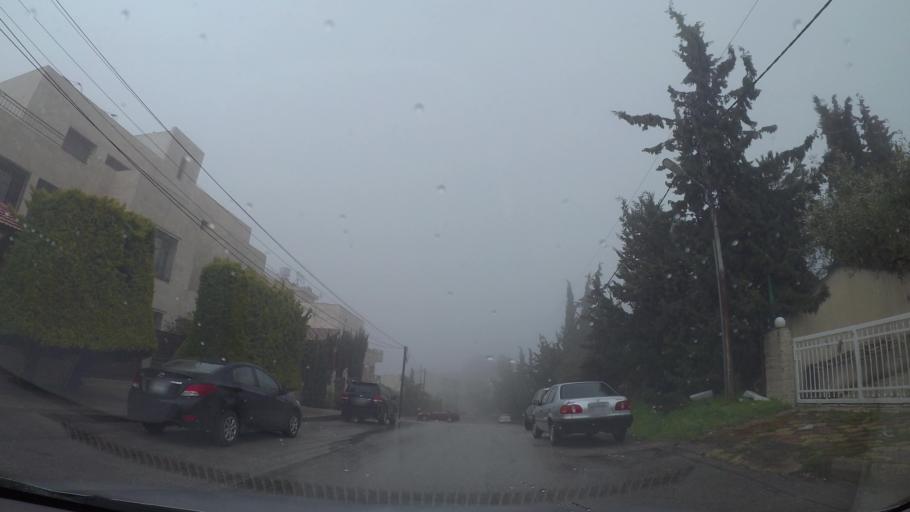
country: JO
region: Amman
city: Wadi as Sir
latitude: 31.9966
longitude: 35.8216
